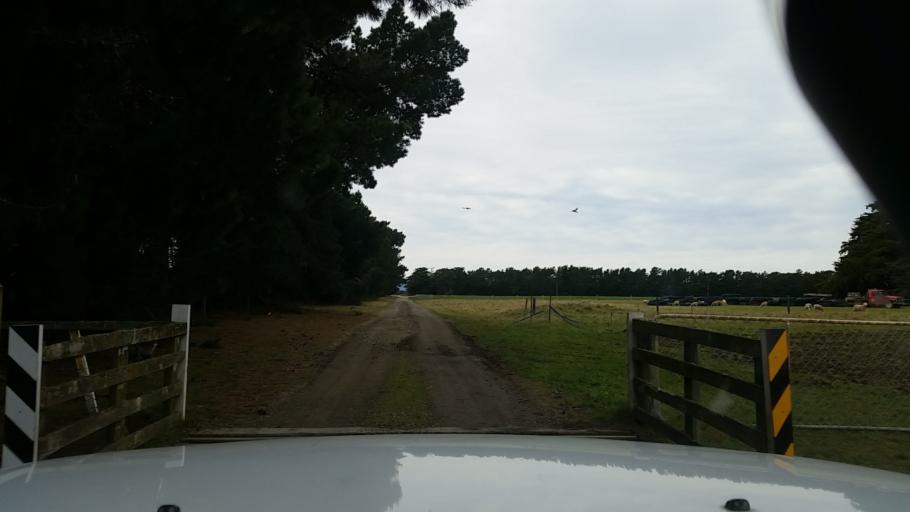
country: NZ
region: Canterbury
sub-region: Selwyn District
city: Lincoln
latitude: -43.8355
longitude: 172.4897
